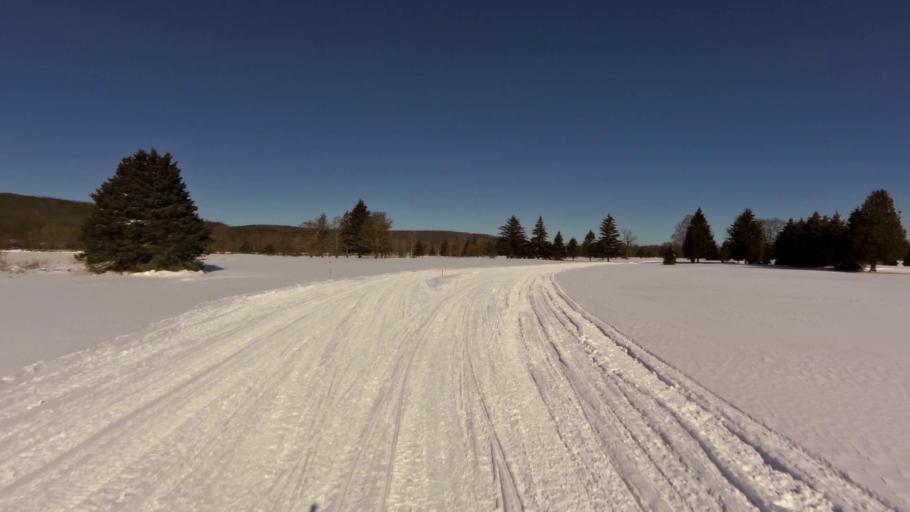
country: US
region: New York
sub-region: Cattaraugus County
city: Franklinville
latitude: 42.3559
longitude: -78.4547
